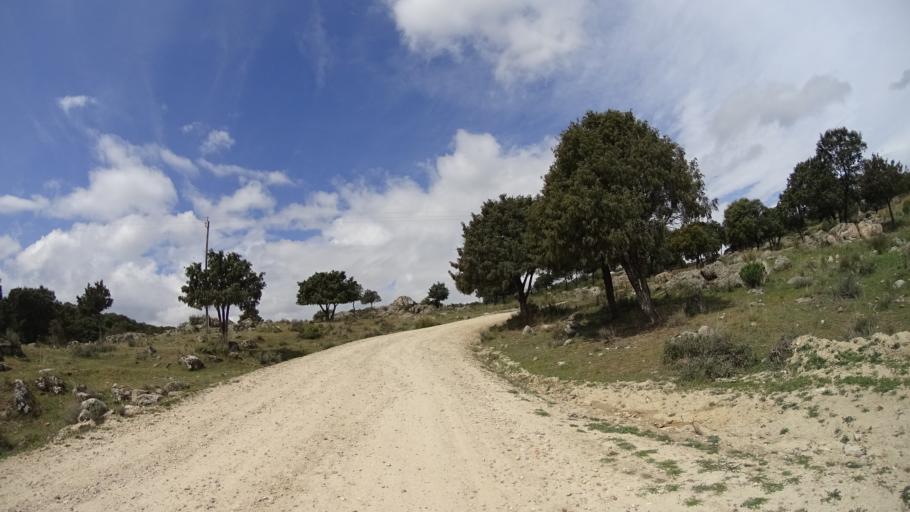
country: ES
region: Madrid
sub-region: Provincia de Madrid
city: Hoyo de Manzanares
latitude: 40.6203
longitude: -3.8834
